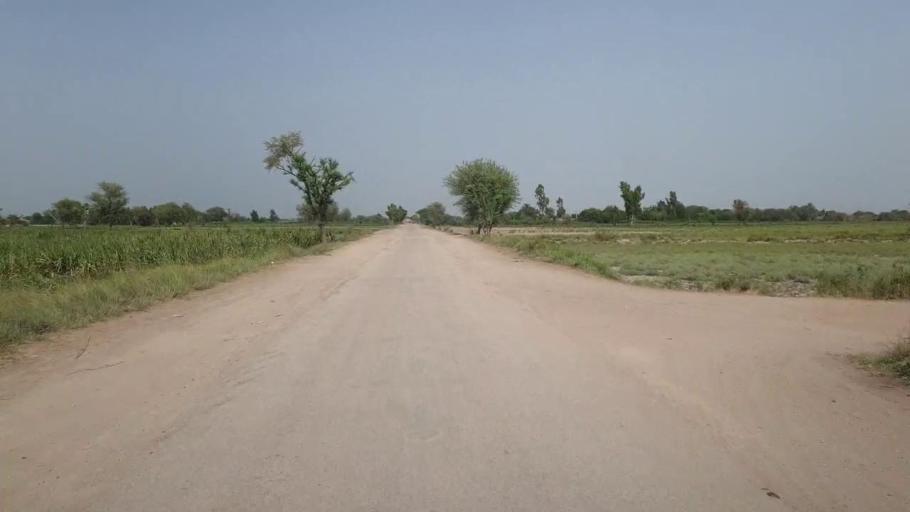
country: PK
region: Sindh
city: Daulatpur
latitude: 26.5485
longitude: 68.0041
